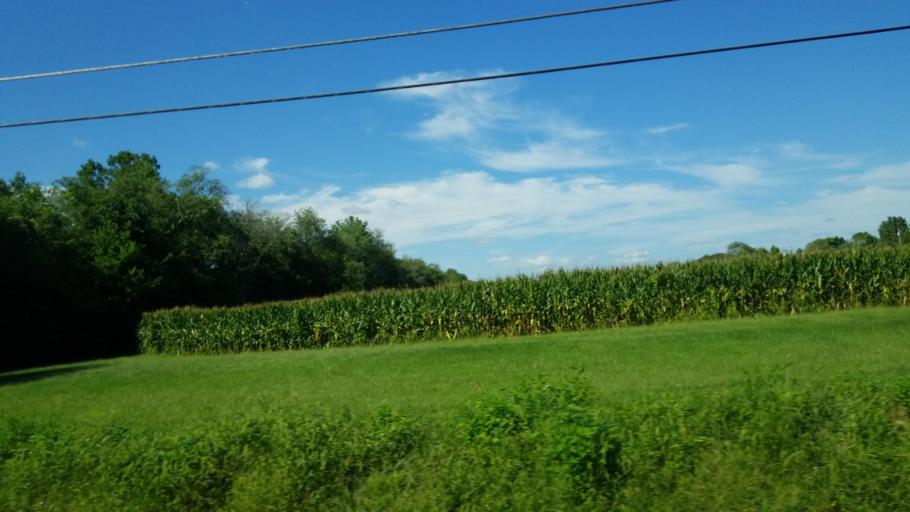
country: US
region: Illinois
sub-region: Williamson County
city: Marion
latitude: 37.7408
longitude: -88.9074
